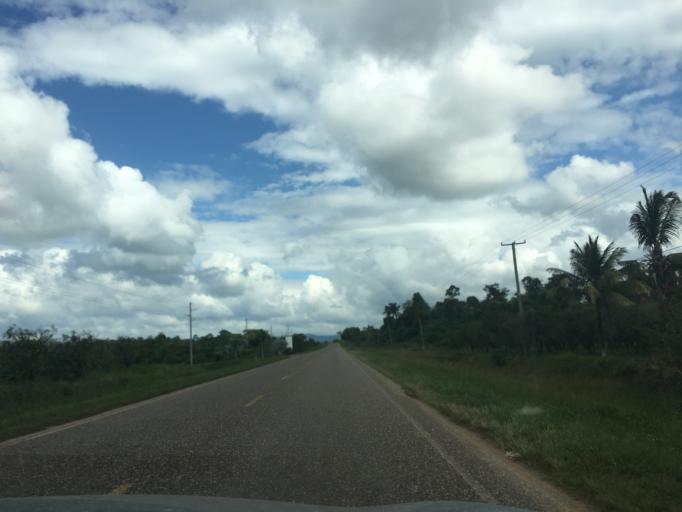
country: BZ
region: Stann Creek
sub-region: Dangriga
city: Dangriga
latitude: 16.8570
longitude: -88.3464
